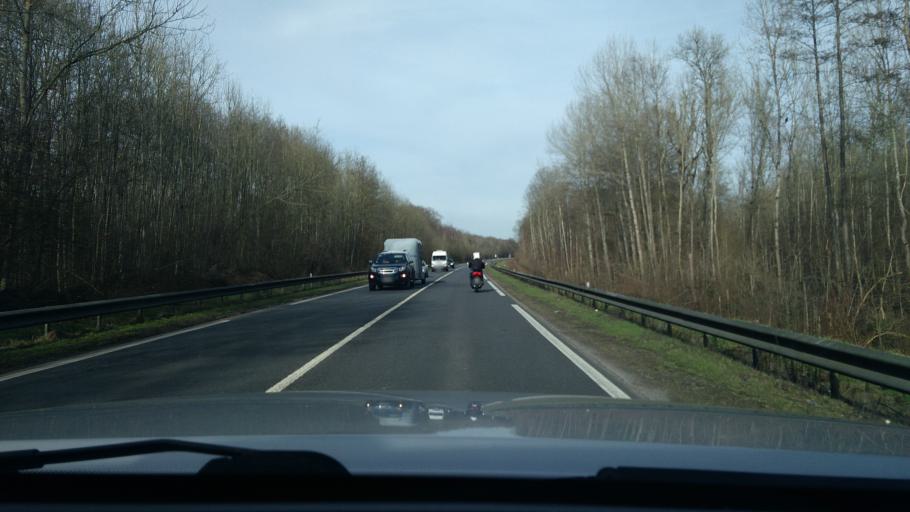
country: FR
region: Ile-de-France
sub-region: Departement de Seine-et-Marne
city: Chaumes-en-Brie
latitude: 48.6875
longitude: 2.8167
